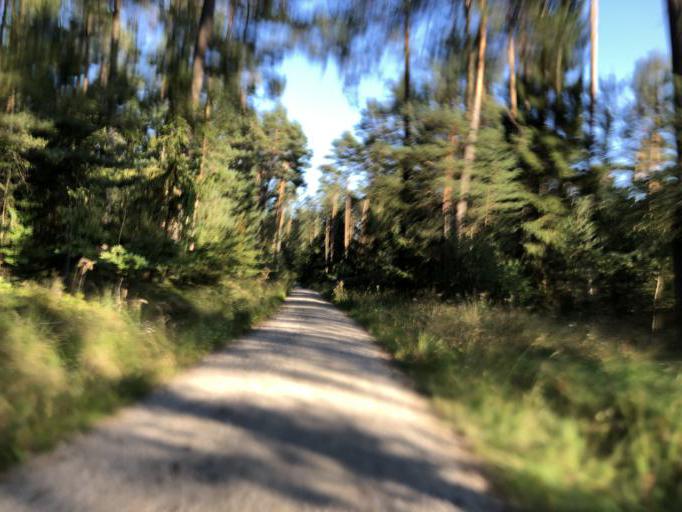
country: DE
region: Bavaria
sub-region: Regierungsbezirk Mittelfranken
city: Kalchreuth
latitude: 49.5469
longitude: 11.0957
